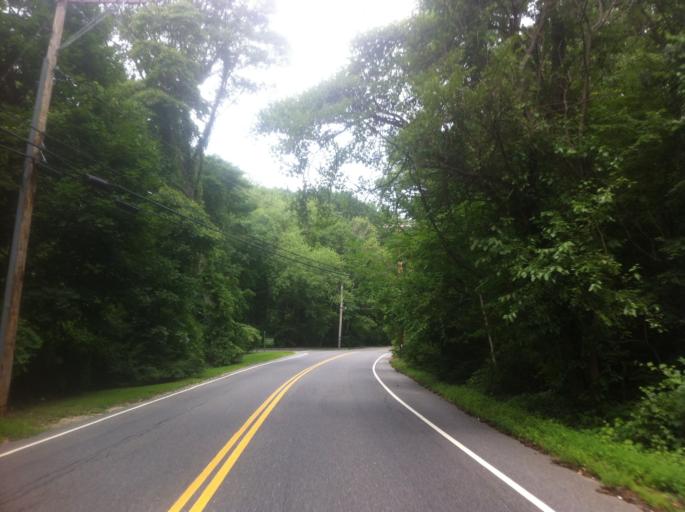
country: US
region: New York
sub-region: Nassau County
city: Oyster Bay Cove
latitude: 40.8576
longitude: -73.5177
